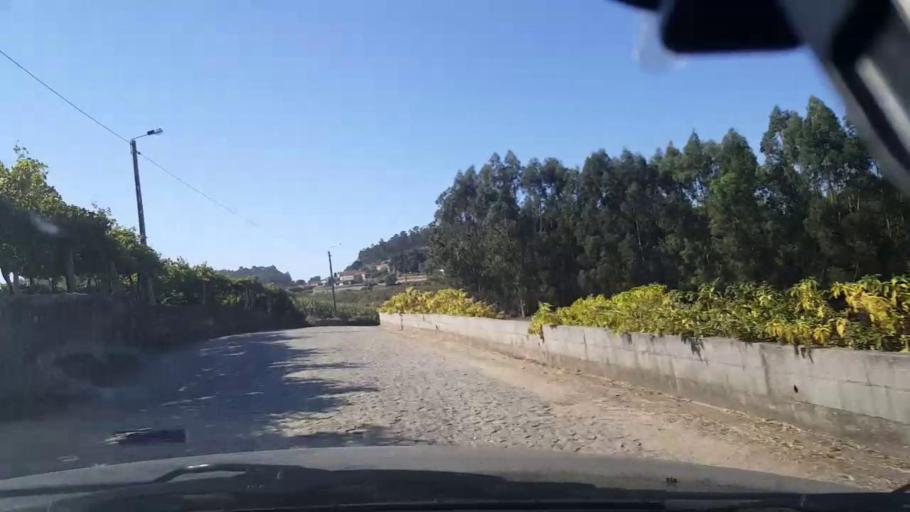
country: PT
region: Braga
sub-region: Vila Nova de Famalicao
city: Ribeirao
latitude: 41.3795
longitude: -8.6382
